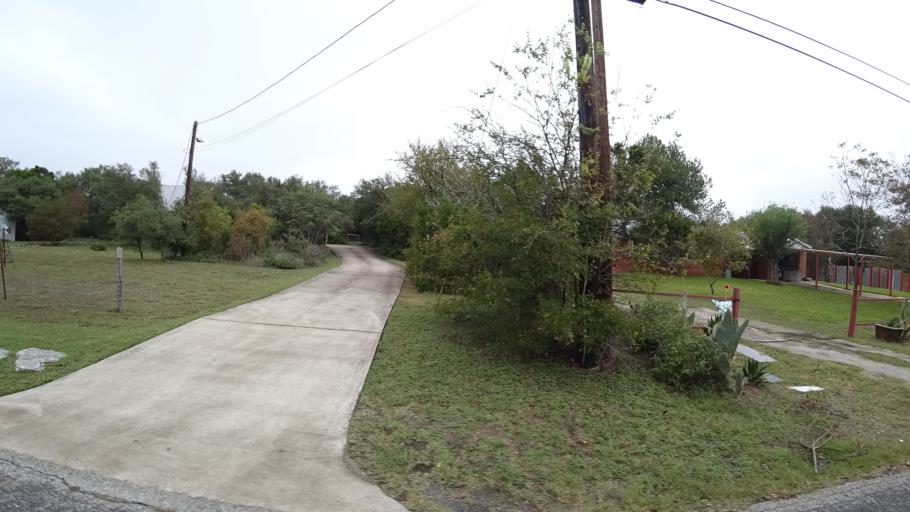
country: US
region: Texas
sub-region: Travis County
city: Barton Creek
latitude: 30.2361
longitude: -97.9024
